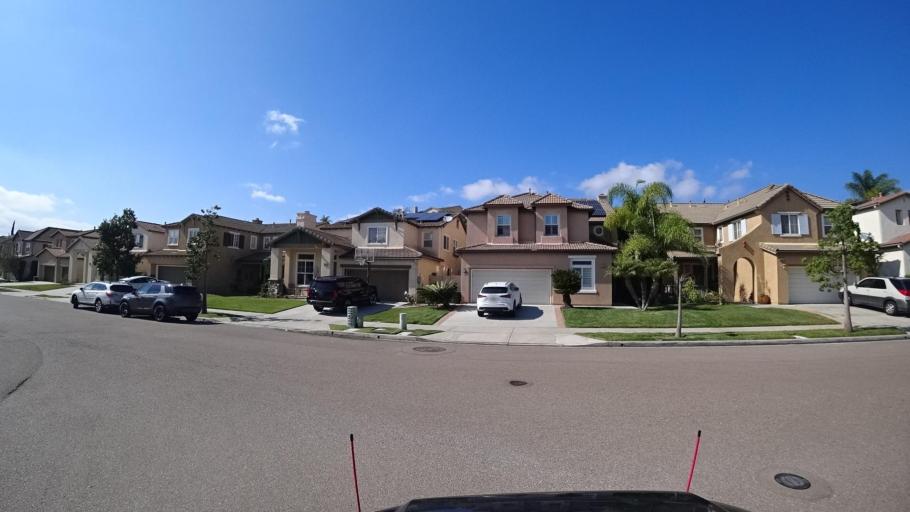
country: US
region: California
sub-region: San Diego County
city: Fairbanks Ranch
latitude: 33.0062
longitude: -117.1135
